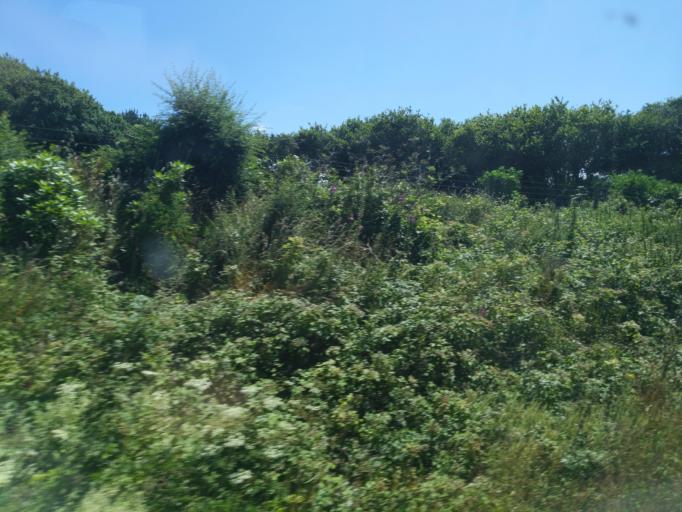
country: GB
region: England
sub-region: Cornwall
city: Saint Stephen
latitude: 50.3320
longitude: -4.8495
